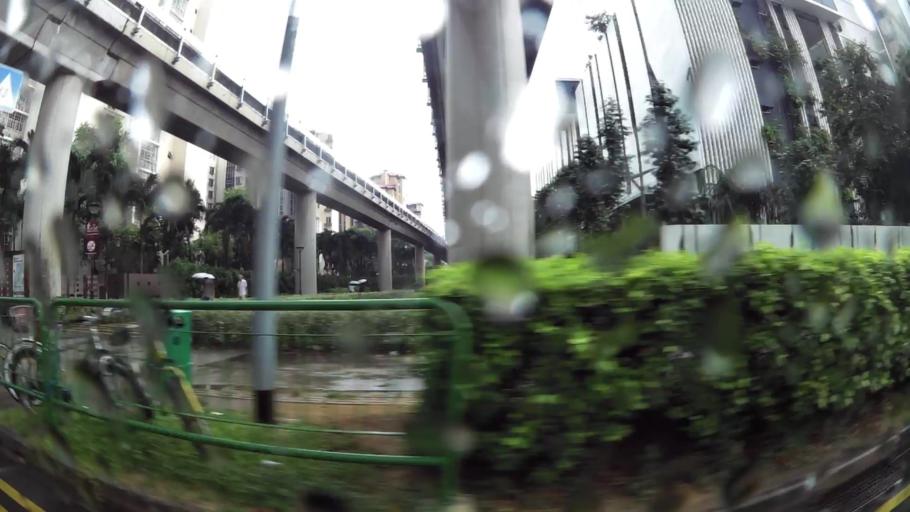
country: SG
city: Singapore
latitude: 1.3424
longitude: 103.9539
